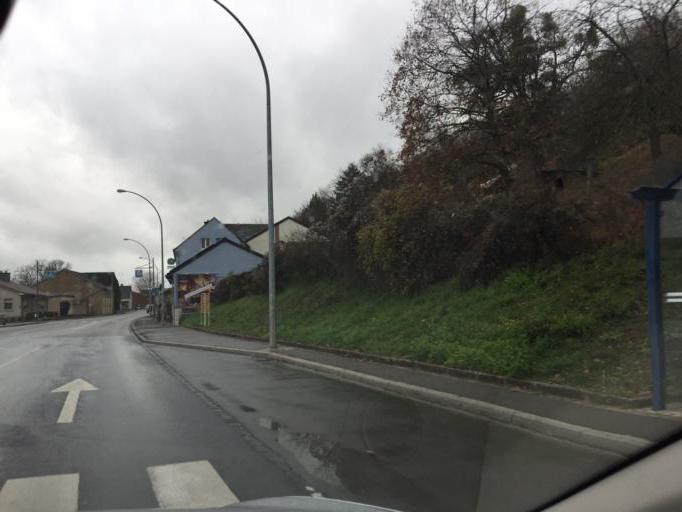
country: LU
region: Diekirch
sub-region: Canton de Diekirch
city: Diekirch
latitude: 49.8697
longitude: 6.1817
